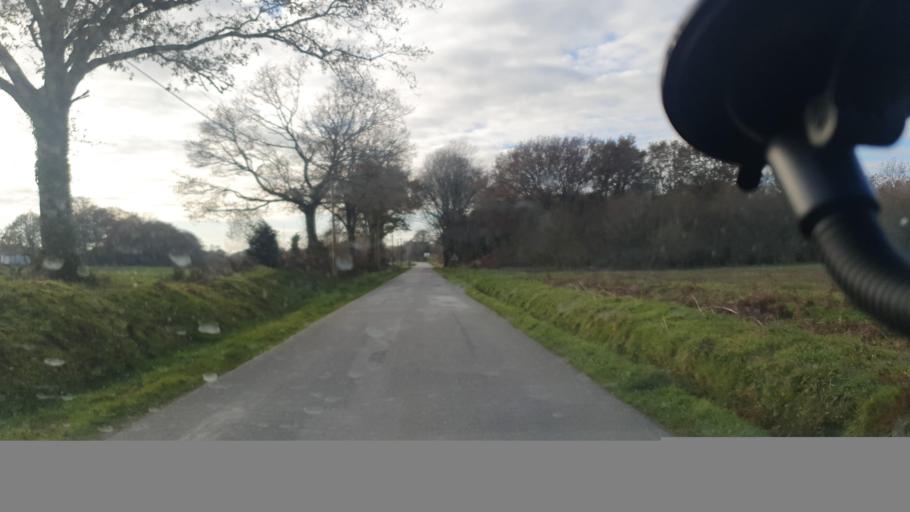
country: FR
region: Brittany
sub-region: Departement du Finistere
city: Briec
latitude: 48.1161
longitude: -4.0184
